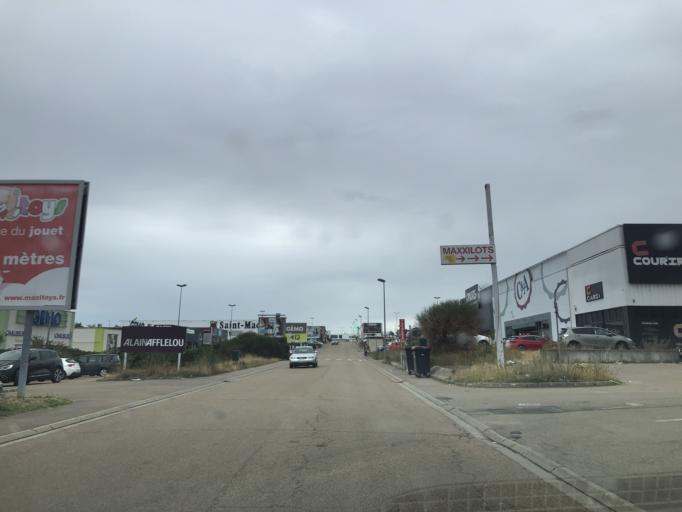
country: FR
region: Bourgogne
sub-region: Departement de l'Yonne
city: Auxerre
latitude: 47.8143
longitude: 3.5716
